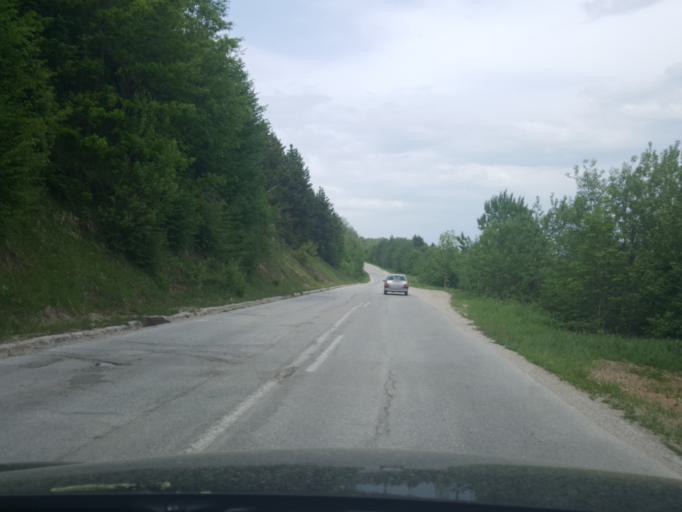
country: RS
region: Central Serbia
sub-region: Zlatiborski Okrug
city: Bajina Basta
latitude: 44.0961
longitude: 19.6662
